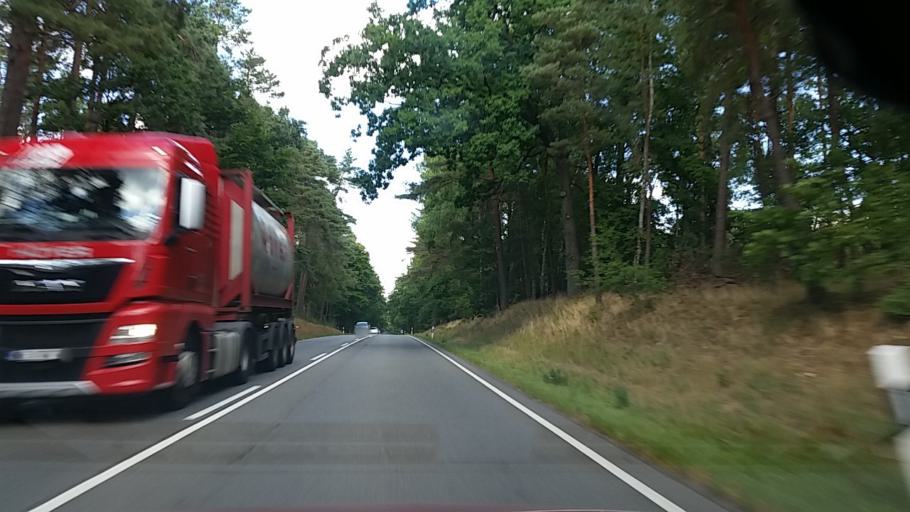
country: DE
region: Lower Saxony
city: Suderburg
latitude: 52.8669
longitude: 10.4936
